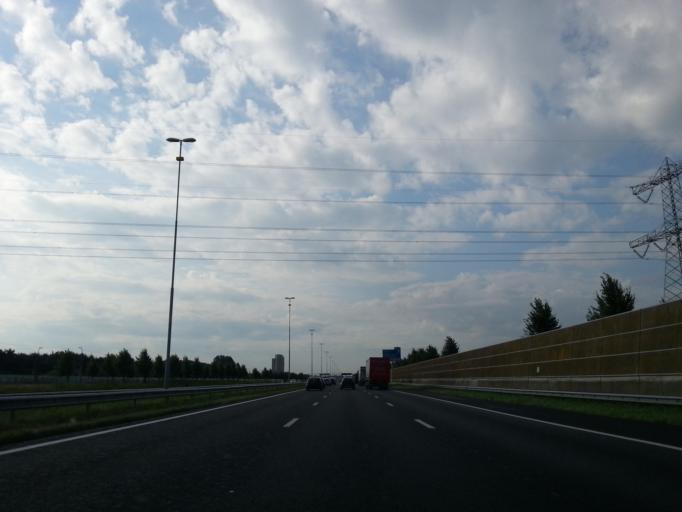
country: NL
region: North Brabant
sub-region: Gemeente Breda
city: Breda
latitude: 51.6195
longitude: 4.7104
